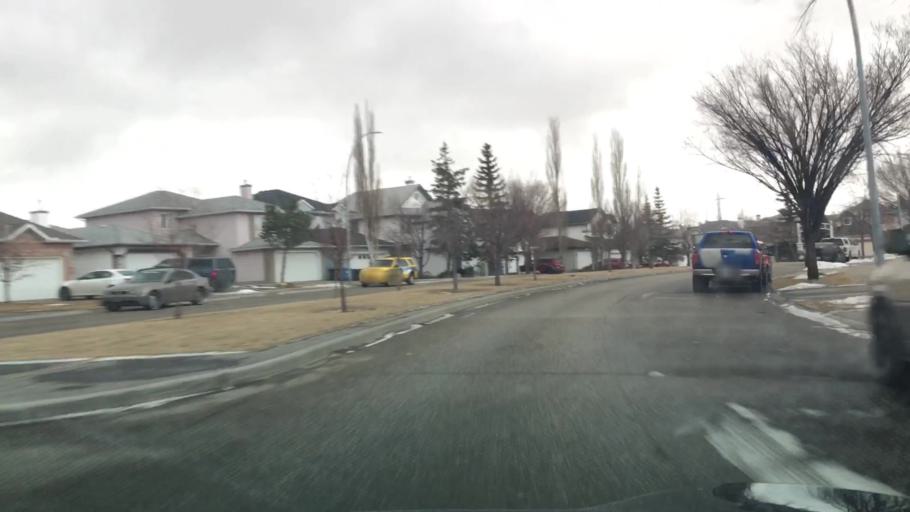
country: CA
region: Alberta
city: Calgary
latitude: 51.1478
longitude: -114.1191
